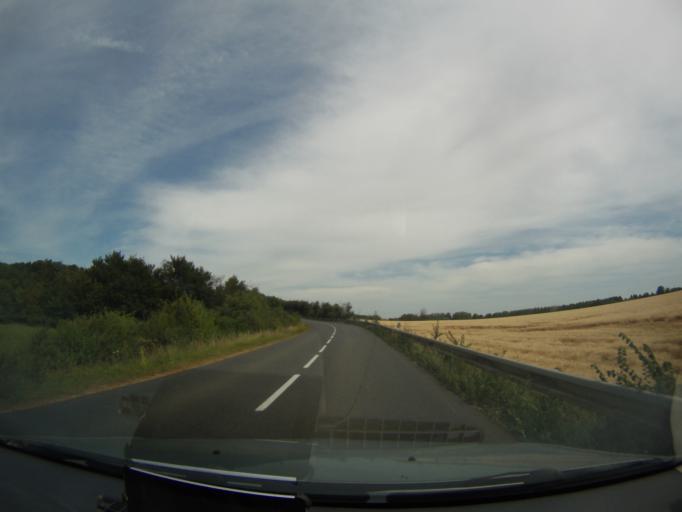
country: FR
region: Poitou-Charentes
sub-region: Departement de la Vienne
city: Saint-Jean-de-Sauves
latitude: 46.8036
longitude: 0.0558
